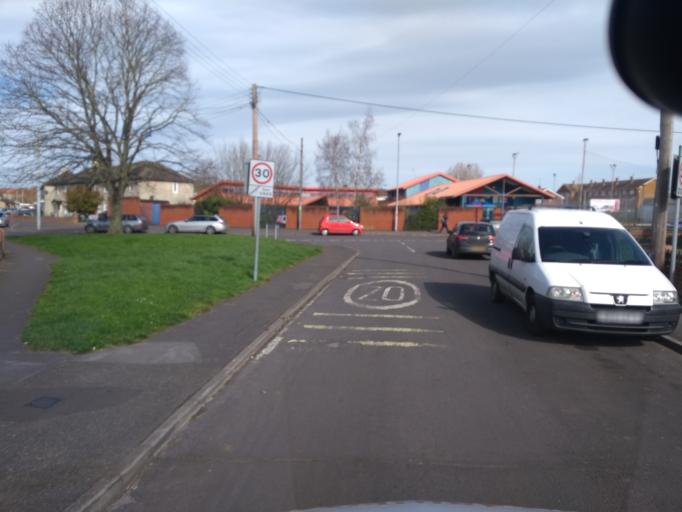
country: GB
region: England
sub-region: Somerset
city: Bridgwater
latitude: 51.1303
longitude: -2.9845
